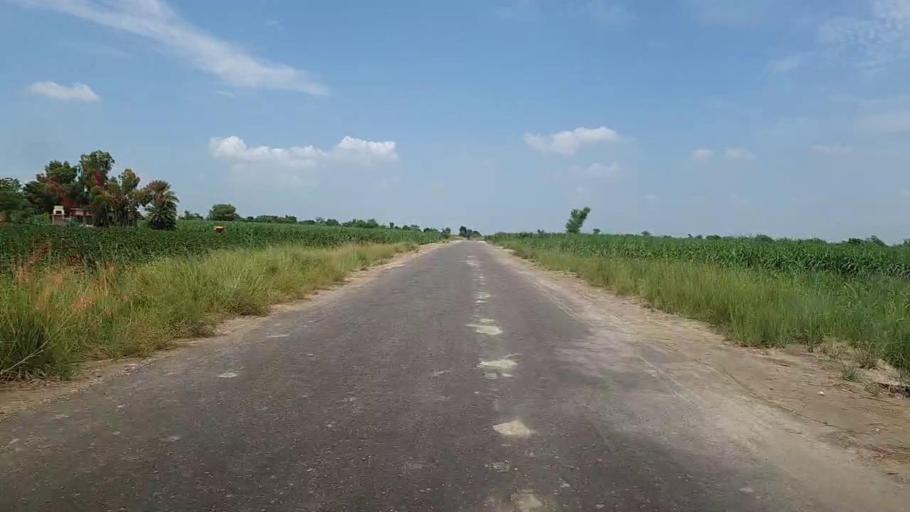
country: PK
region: Sindh
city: Bhiria
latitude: 26.9356
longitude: 68.2172
